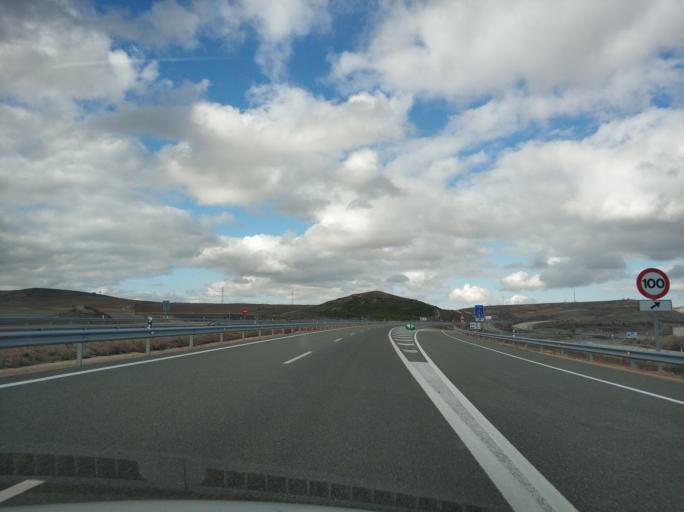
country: ES
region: Castille and Leon
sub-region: Provincia de Soria
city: Yelo
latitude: 41.2161
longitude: -2.4696
